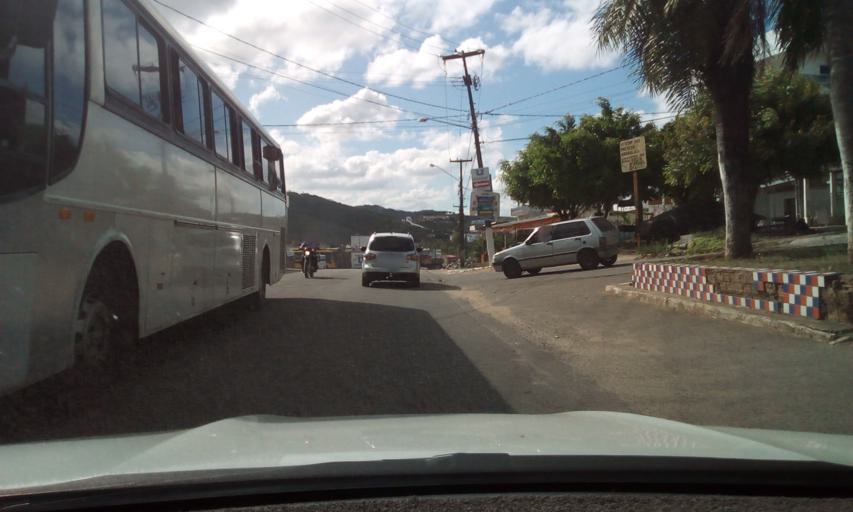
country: BR
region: Paraiba
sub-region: Guarabira
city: Guarabira
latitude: -6.8636
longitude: -35.4945
